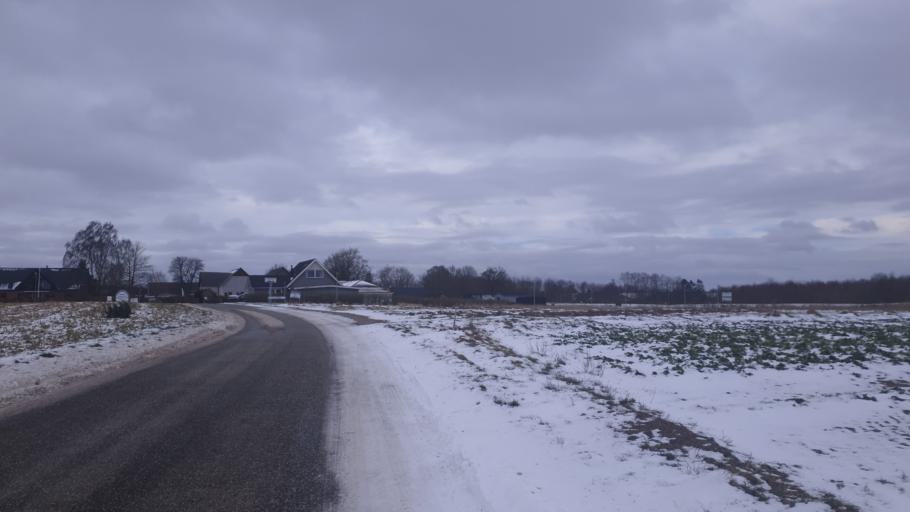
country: DK
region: Central Jutland
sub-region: Hedensted Kommune
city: Hedensted
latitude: 55.8006
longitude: 9.7058
